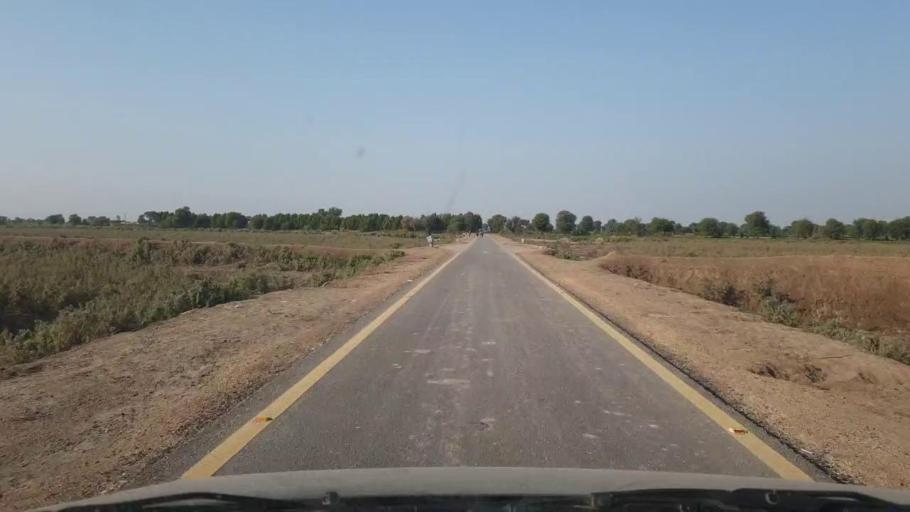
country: PK
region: Sindh
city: Samaro
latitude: 25.2955
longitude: 69.3488
